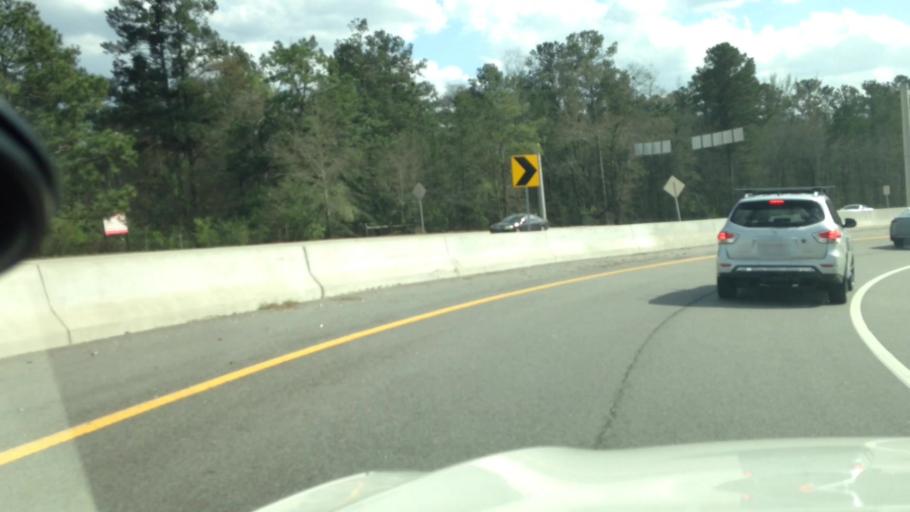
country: US
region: Georgia
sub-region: Columbia County
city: Martinez
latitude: 33.4497
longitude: -82.0719
